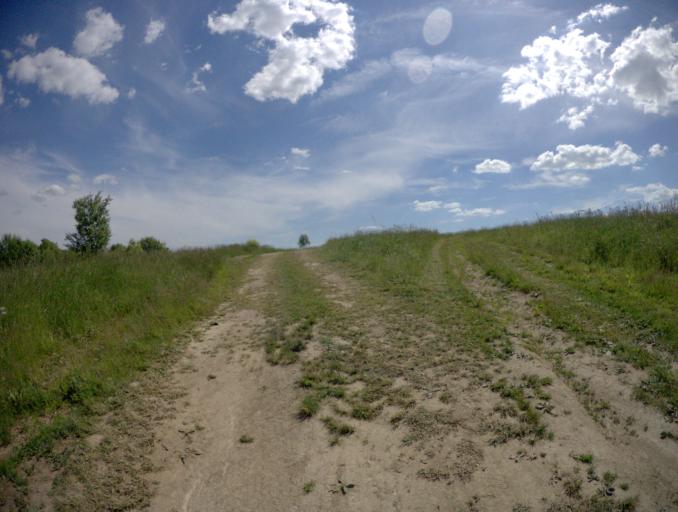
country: RU
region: Ivanovo
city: Gavrilov Posad
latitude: 56.3602
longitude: 40.0799
